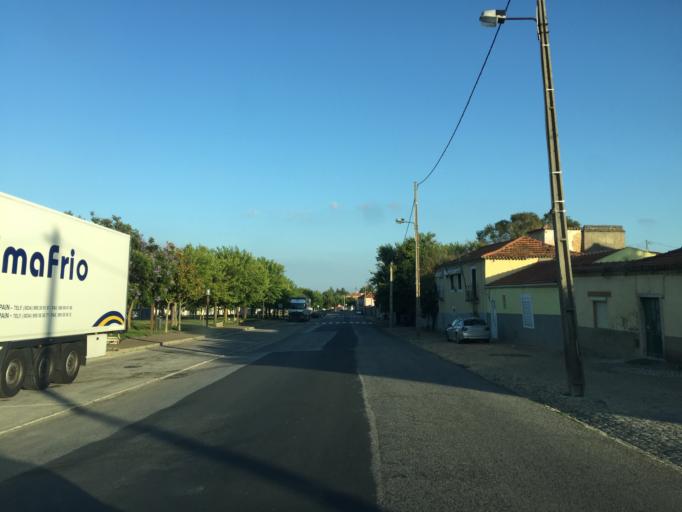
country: PT
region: Lisbon
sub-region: Odivelas
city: Olival do Basto
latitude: 38.7870
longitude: -9.1445
